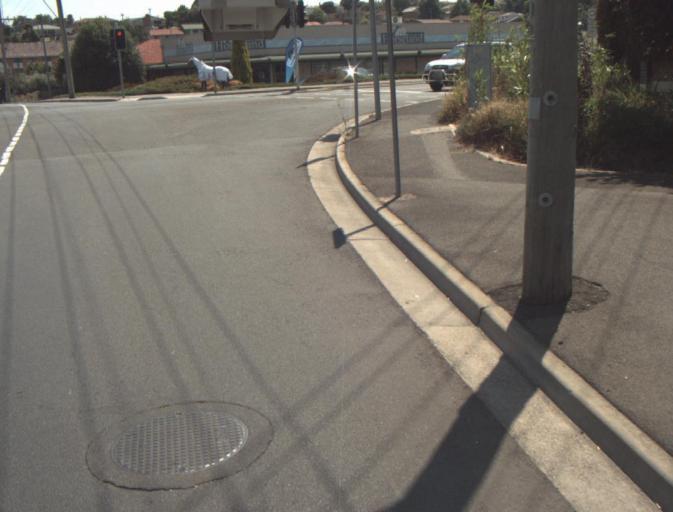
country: AU
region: Tasmania
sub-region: Launceston
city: East Launceston
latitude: -41.4601
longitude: 147.1558
